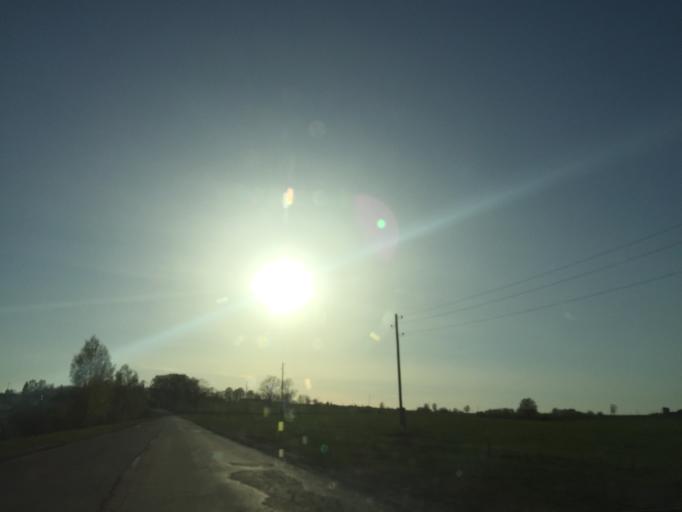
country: LV
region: Koknese
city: Koknese
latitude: 56.7246
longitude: 25.5003
